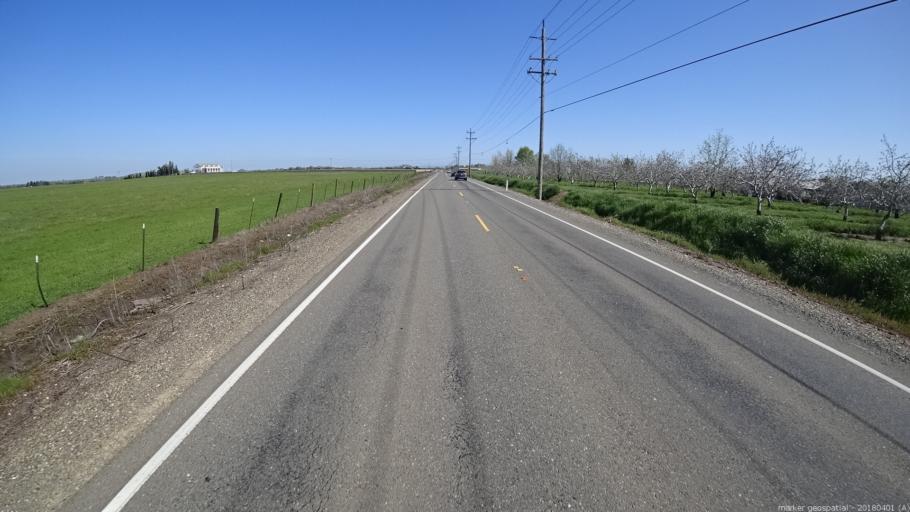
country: US
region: California
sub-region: Sacramento County
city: Rancho Murieta
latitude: 38.4718
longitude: -121.1728
